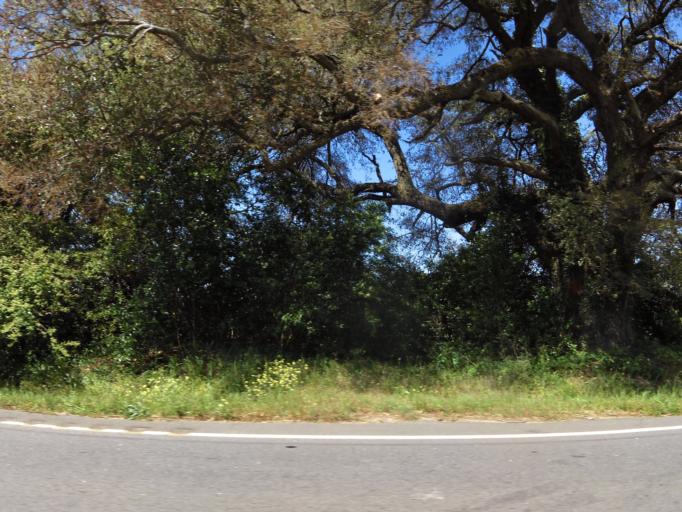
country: US
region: South Carolina
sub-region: Aiken County
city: Aiken
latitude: 33.5350
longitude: -81.6480
